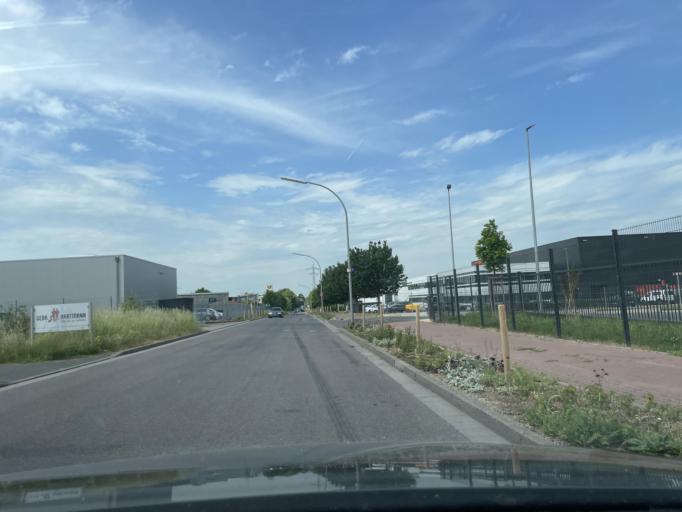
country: DE
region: North Rhine-Westphalia
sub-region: Regierungsbezirk Dusseldorf
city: Juchen
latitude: 51.1157
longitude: 6.4447
